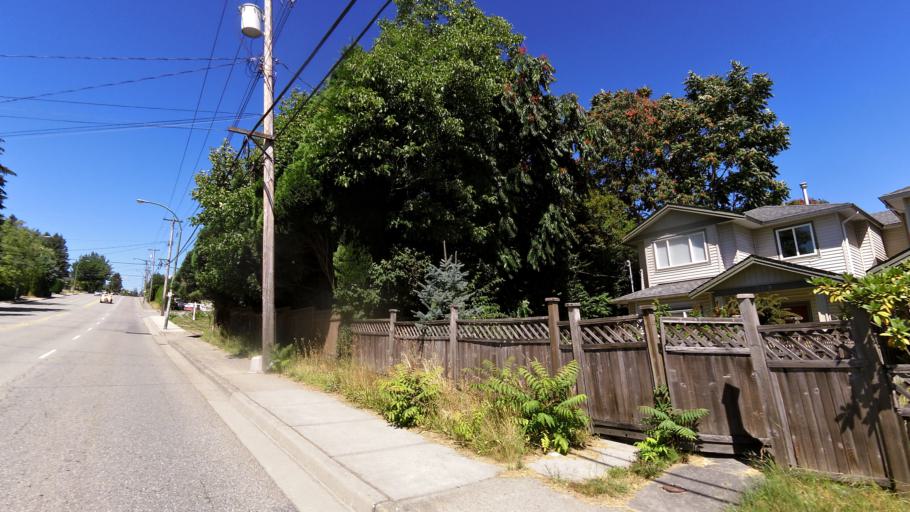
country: CA
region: British Columbia
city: Port Moody
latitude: 49.2410
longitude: -122.8729
